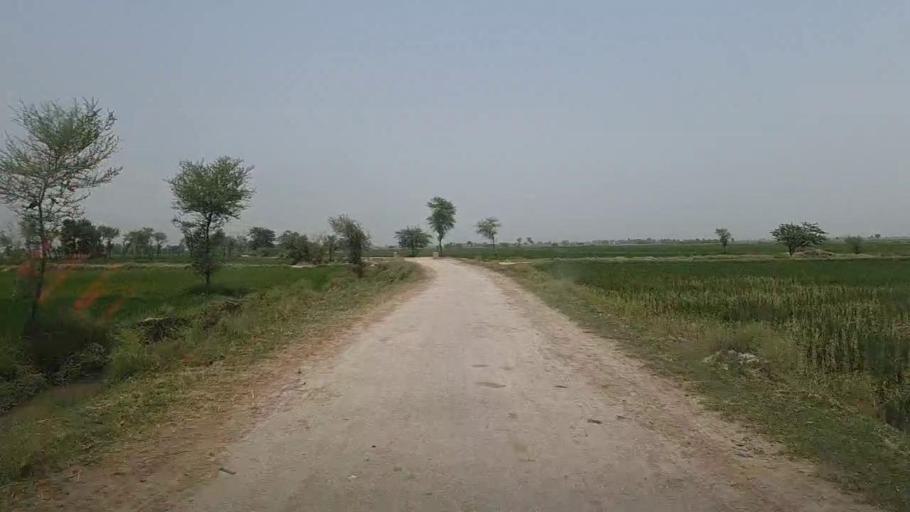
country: PK
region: Sindh
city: Sita Road
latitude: 27.0613
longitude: 67.8491
